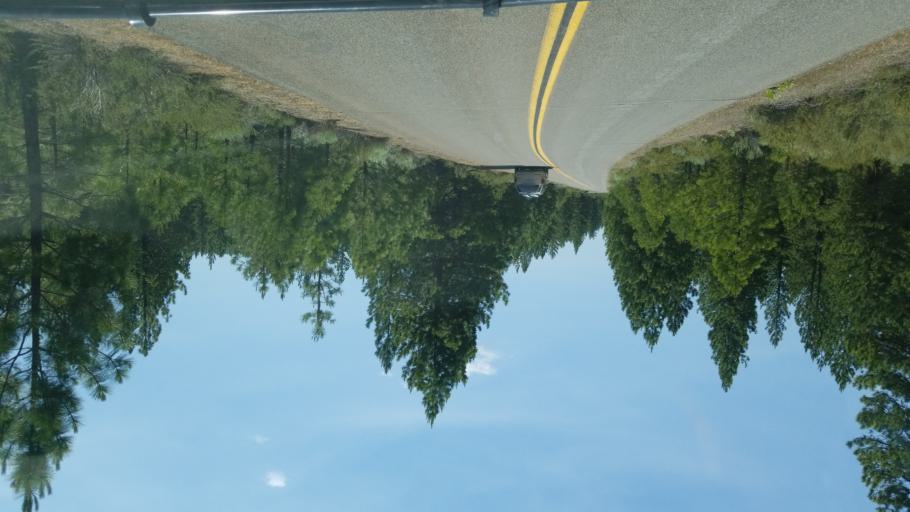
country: US
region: California
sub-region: Lassen County
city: Susanville
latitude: 40.5694
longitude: -120.8425
